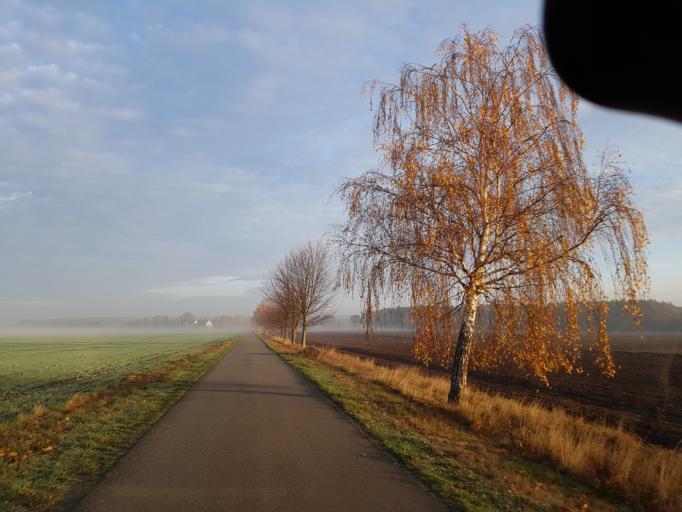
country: DE
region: Saxony-Anhalt
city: Elster
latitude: 51.8724
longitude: 12.8474
